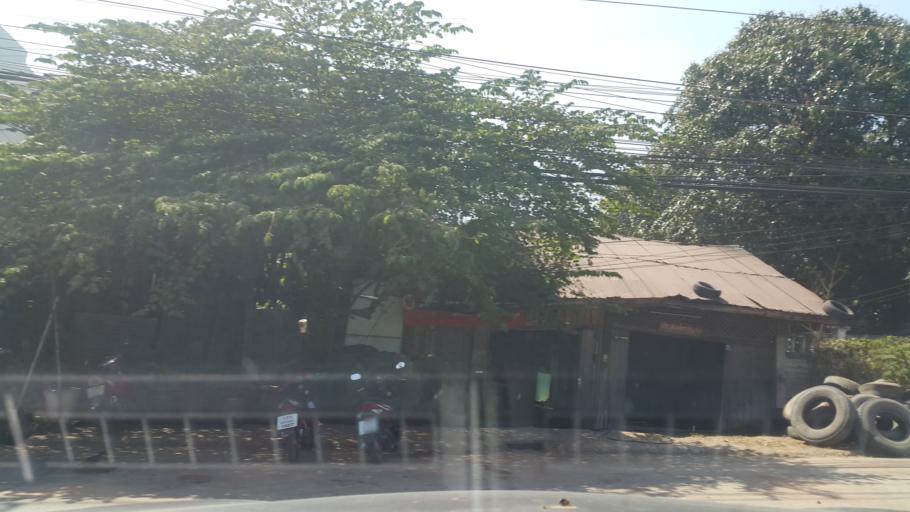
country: TH
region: Nakhon Ratchasima
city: Bua Yai
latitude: 15.5940
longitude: 102.4193
